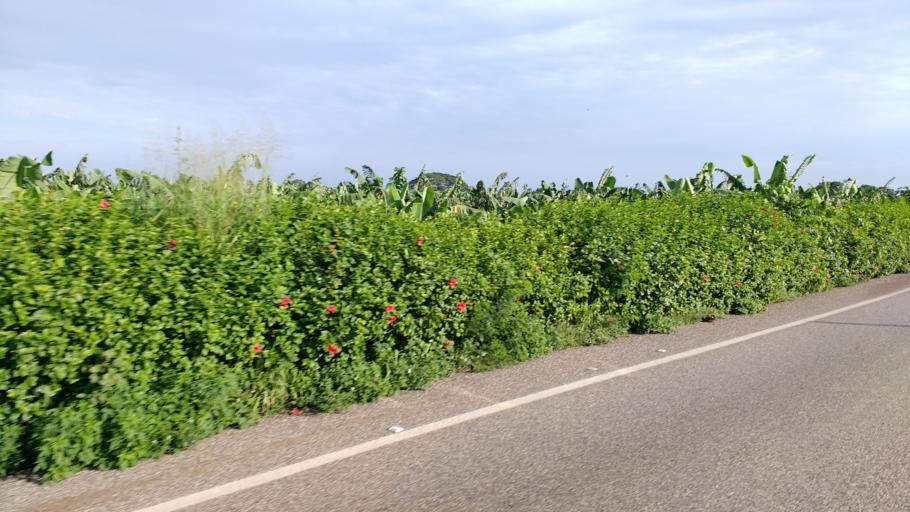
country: MX
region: Tabasco
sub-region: Teapa
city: Eureka y Belen
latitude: 17.6156
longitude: -92.9642
